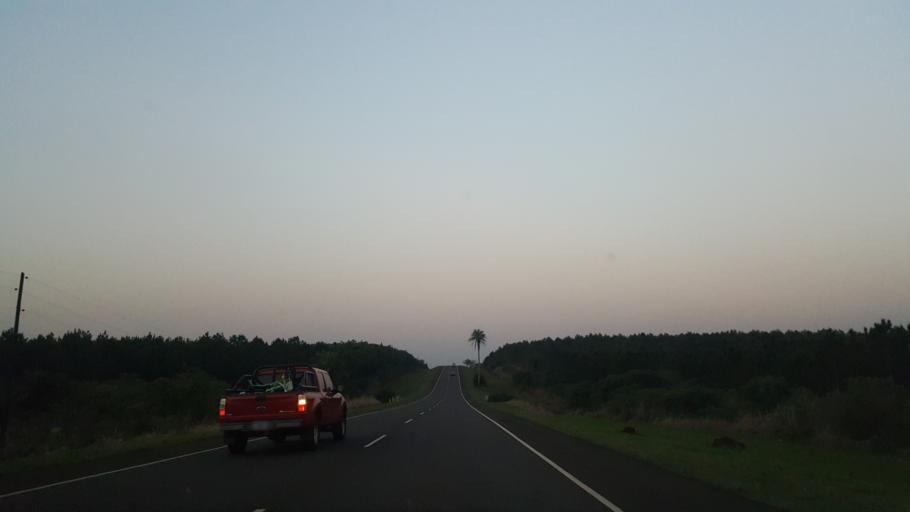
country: AR
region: Misiones
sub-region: Departamento de Capital
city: Posadas
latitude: -27.4396
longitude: -56.0212
